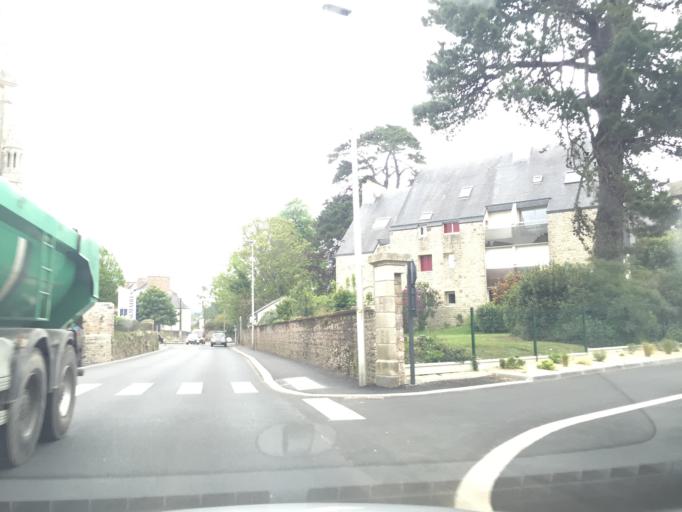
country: FR
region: Brittany
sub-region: Departement des Cotes-d'Armor
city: Paimpol
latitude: 48.7800
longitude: -3.0493
